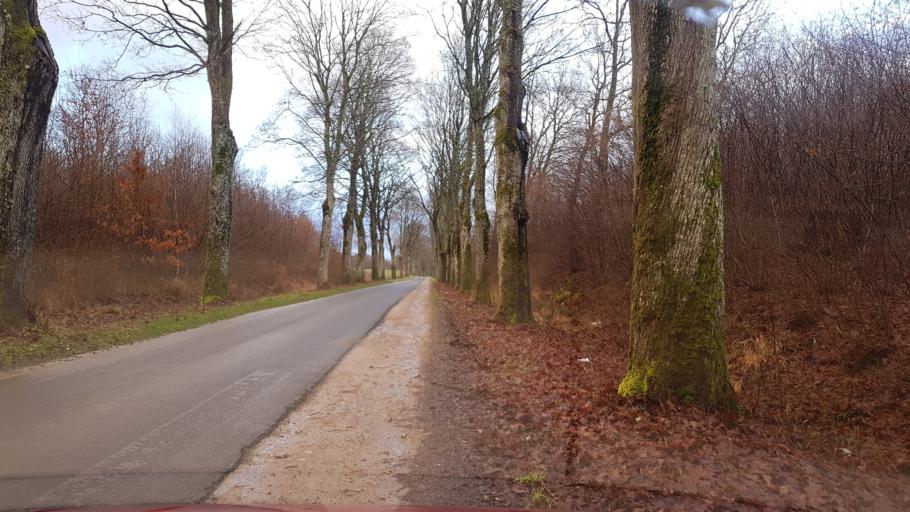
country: PL
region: West Pomeranian Voivodeship
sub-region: Powiat bialogardzki
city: Karlino
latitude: 53.9507
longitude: 15.9064
